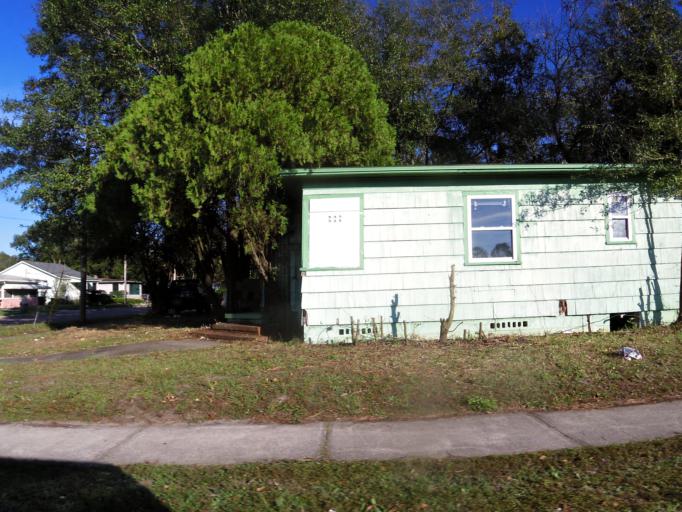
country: US
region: Florida
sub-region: Duval County
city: Jacksonville
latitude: 30.3532
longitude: -81.6863
